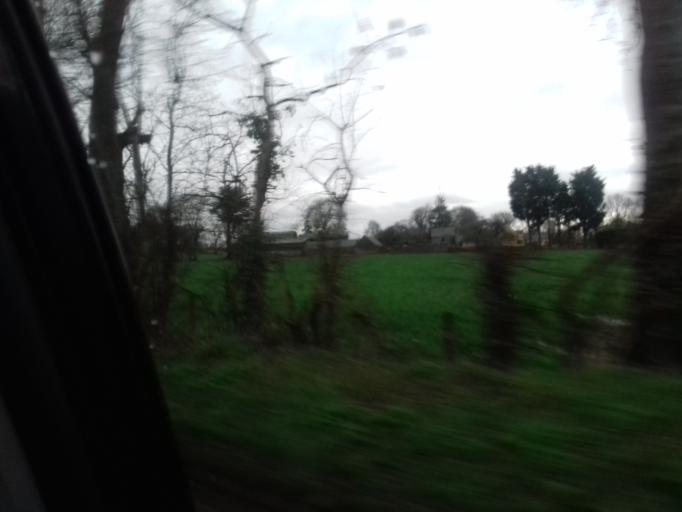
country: IE
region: Leinster
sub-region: County Carlow
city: Bagenalstown
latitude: 52.6705
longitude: -7.0086
